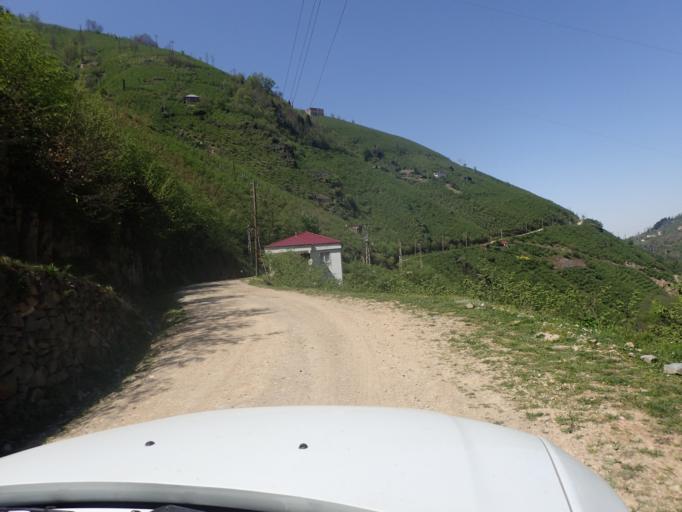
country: TR
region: Ordu
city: Kabaduz
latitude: 40.7388
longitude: 37.8937
